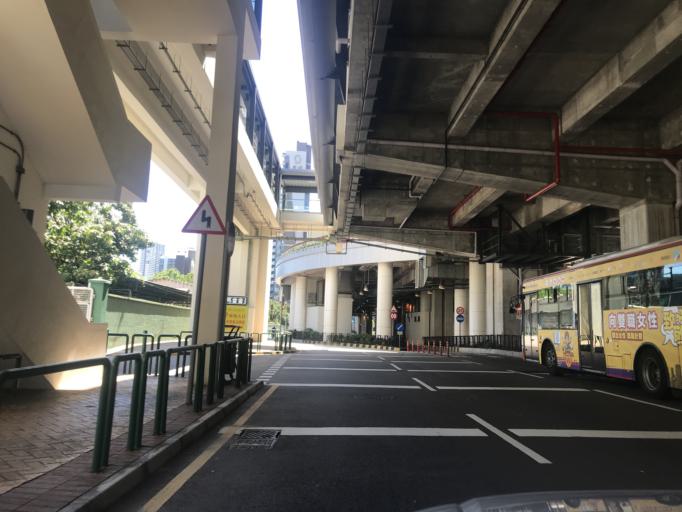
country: MO
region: Macau
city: Macau
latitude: 22.1570
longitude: 113.5473
